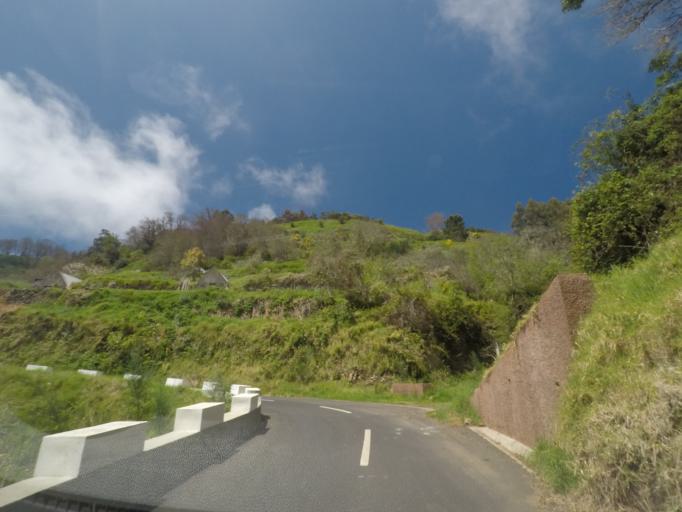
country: PT
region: Madeira
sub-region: Calheta
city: Arco da Calheta
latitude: 32.7289
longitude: -17.1211
